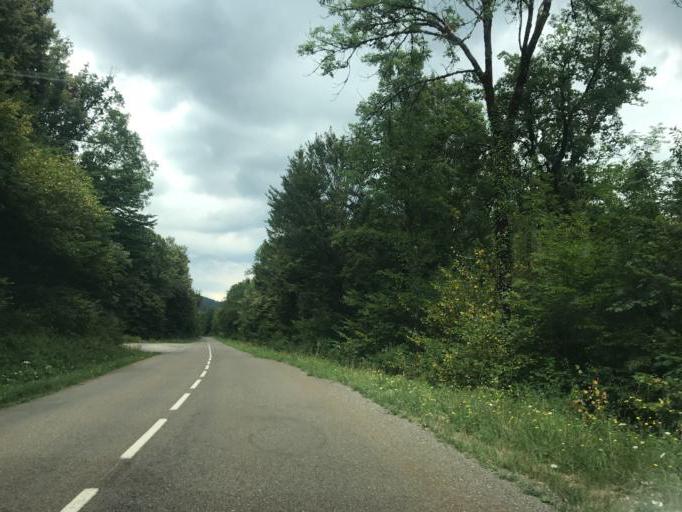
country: FR
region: Franche-Comte
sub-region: Departement du Jura
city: Valfin-les-Saint-Claude
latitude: 46.4525
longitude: 5.8673
